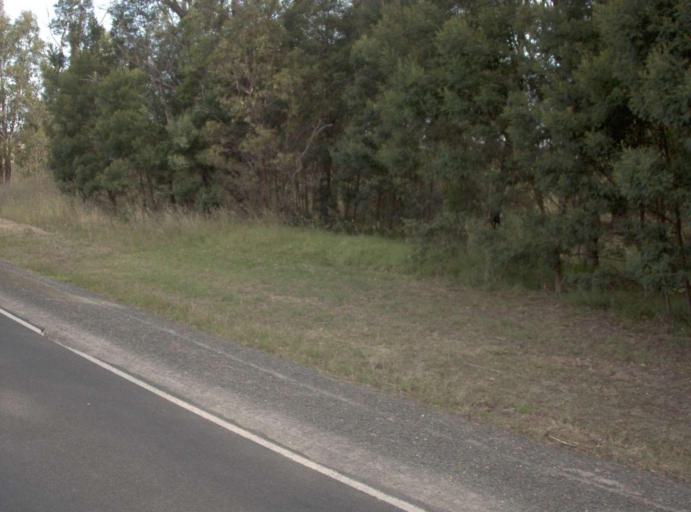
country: AU
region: Victoria
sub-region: Wellington
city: Heyfield
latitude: -38.0592
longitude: 146.6385
